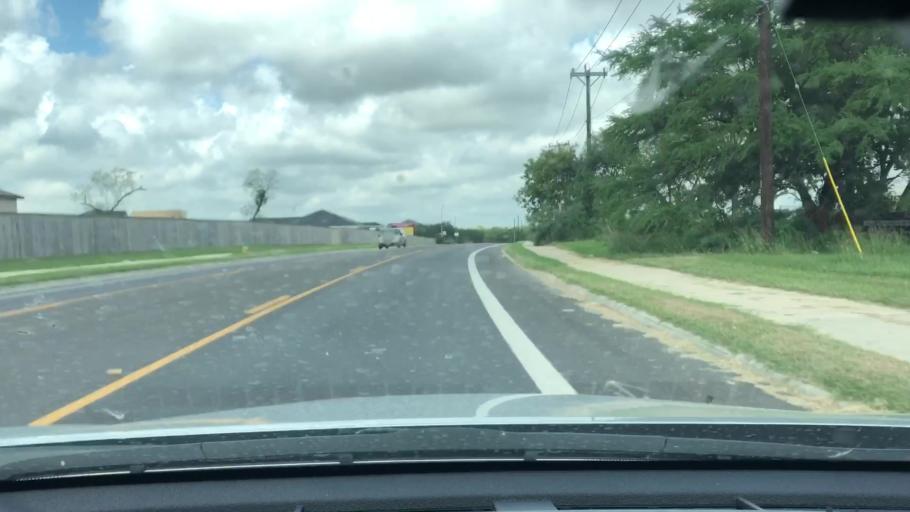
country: US
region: Texas
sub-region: Bexar County
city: Windcrest
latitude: 29.4981
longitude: -98.3653
